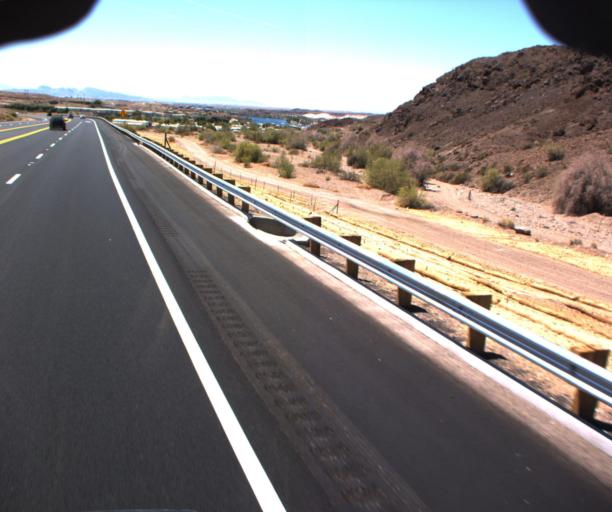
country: US
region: Arizona
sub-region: La Paz County
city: Cienega Springs
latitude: 34.1905
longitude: -114.2106
